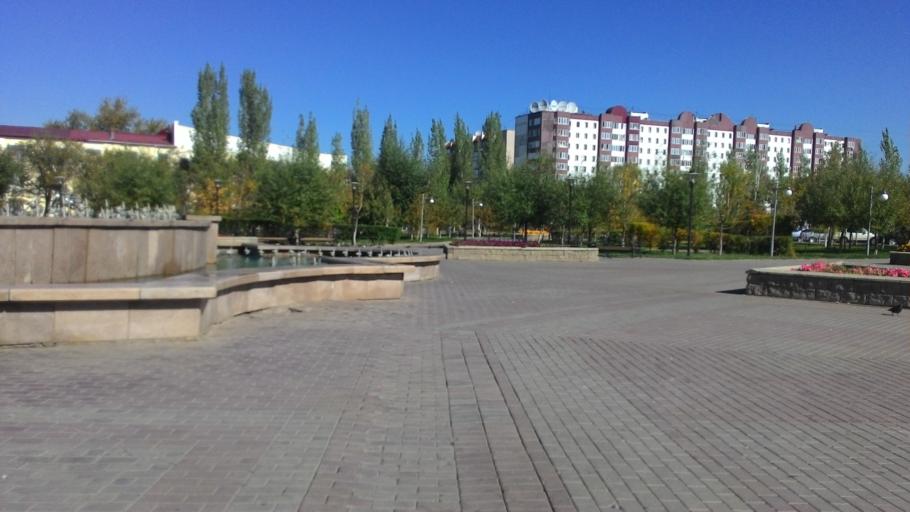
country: KZ
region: Astana Qalasy
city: Astana
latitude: 51.1660
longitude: 71.4154
